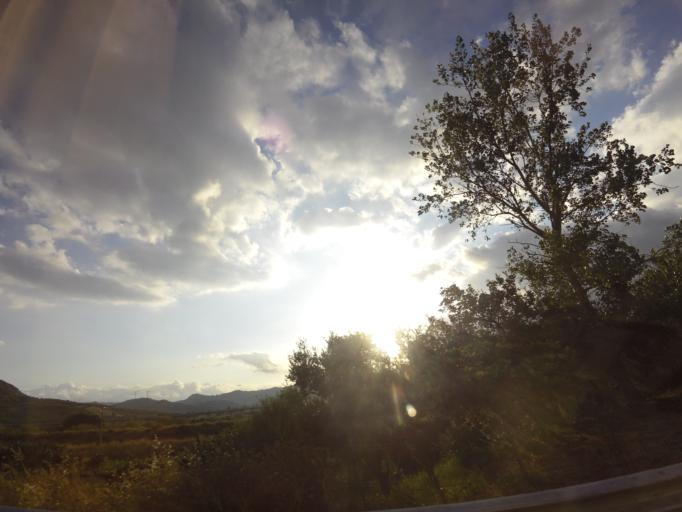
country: IT
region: Calabria
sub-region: Provincia di Catanzaro
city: Catanzaro
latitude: 38.8838
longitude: 16.5552
